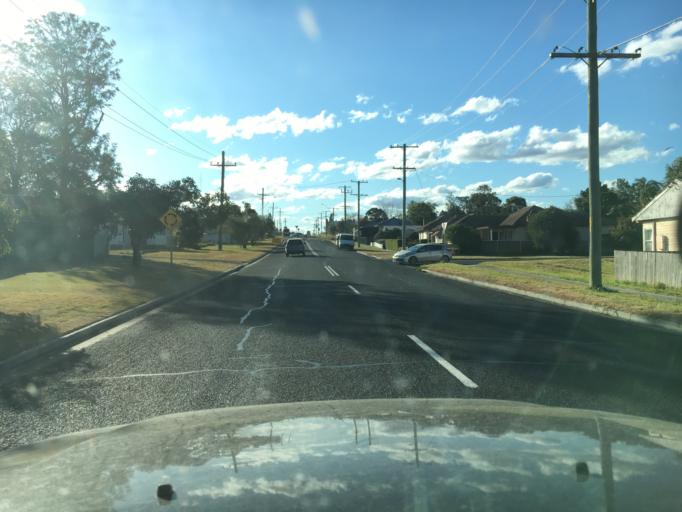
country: AU
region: New South Wales
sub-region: Maitland Municipality
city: East Maitland
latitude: -32.7587
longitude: 151.5848
